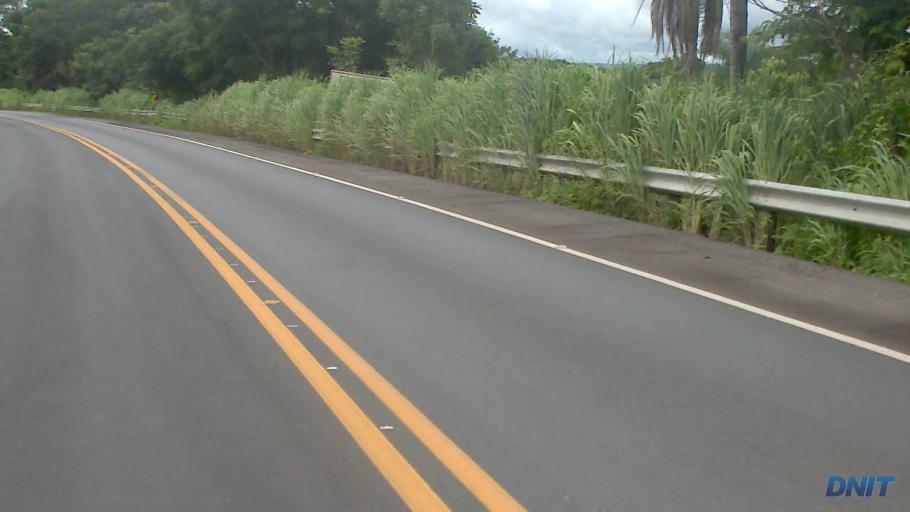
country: BR
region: Goias
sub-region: Posse
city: Posse
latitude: -14.3514
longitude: -46.4410
